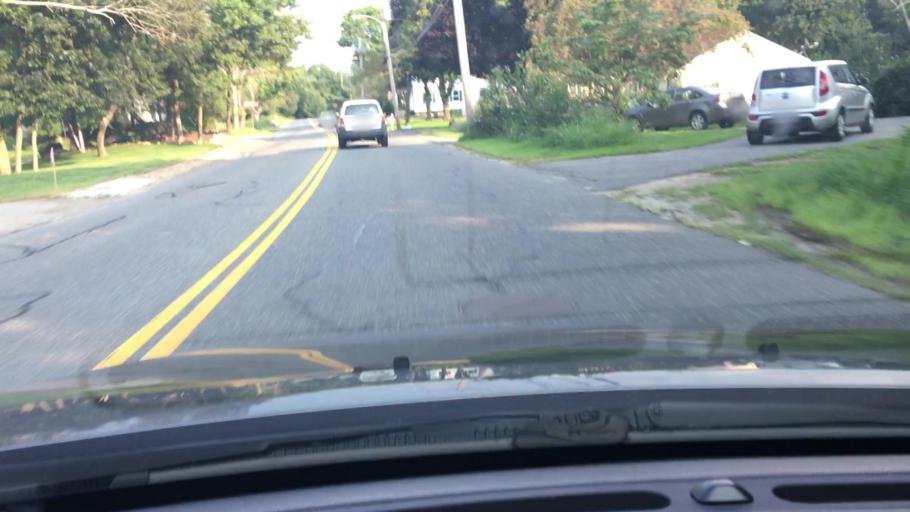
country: US
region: Massachusetts
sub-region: Worcester County
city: Milford
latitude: 42.1764
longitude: -71.5343
